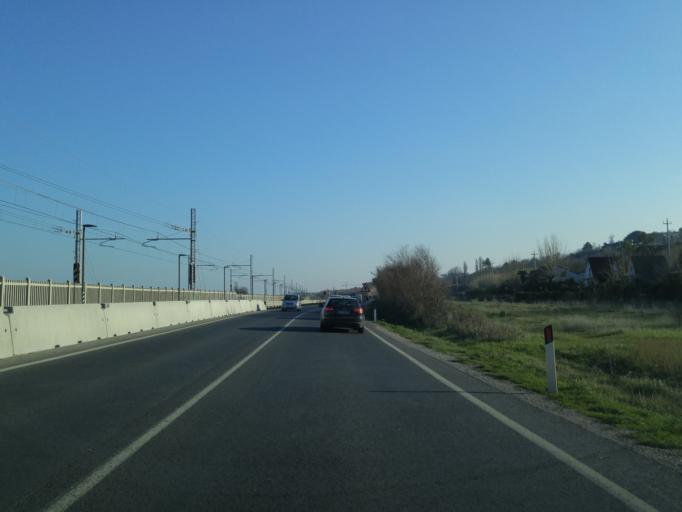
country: IT
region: The Marches
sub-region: Provincia di Pesaro e Urbino
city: Fenile
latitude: 43.8684
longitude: 12.9809
